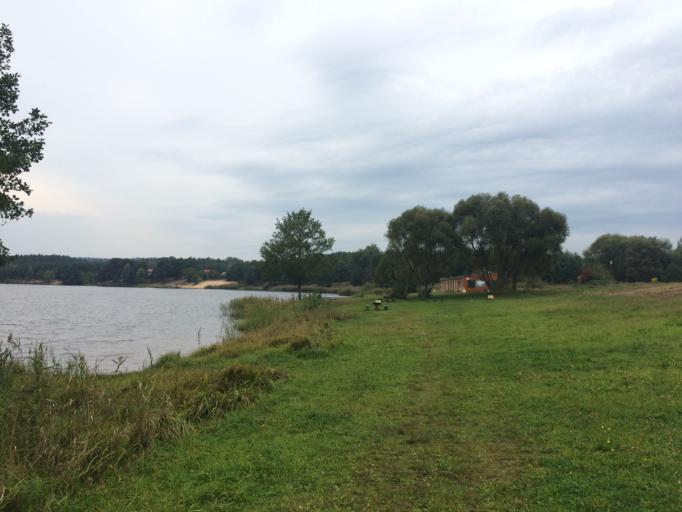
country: PL
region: Swietokrzyskie
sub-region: Powiat starachowicki
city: Starachowice
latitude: 51.0277
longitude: 21.0456
